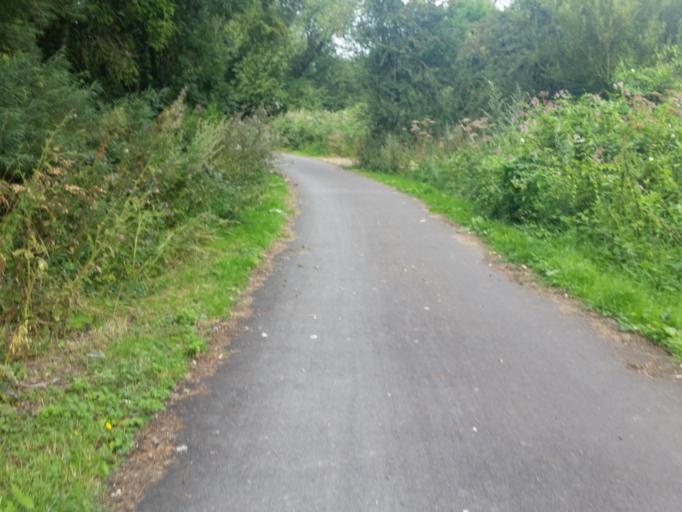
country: GB
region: England
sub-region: Derbyshire
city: Borrowash
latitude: 52.9034
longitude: -1.4259
